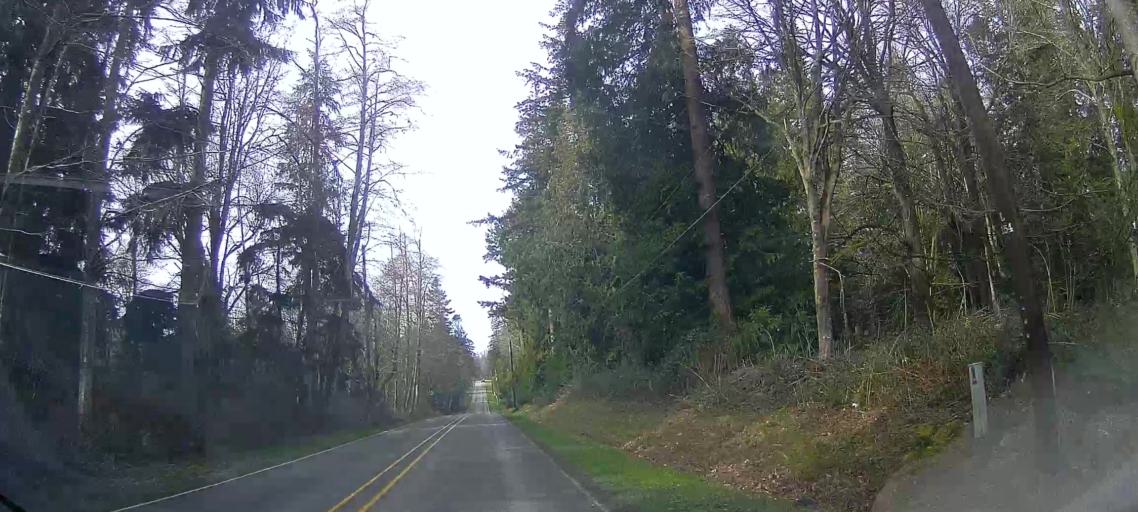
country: US
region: Washington
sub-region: Island County
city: Langley
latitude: 48.0867
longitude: -122.3849
